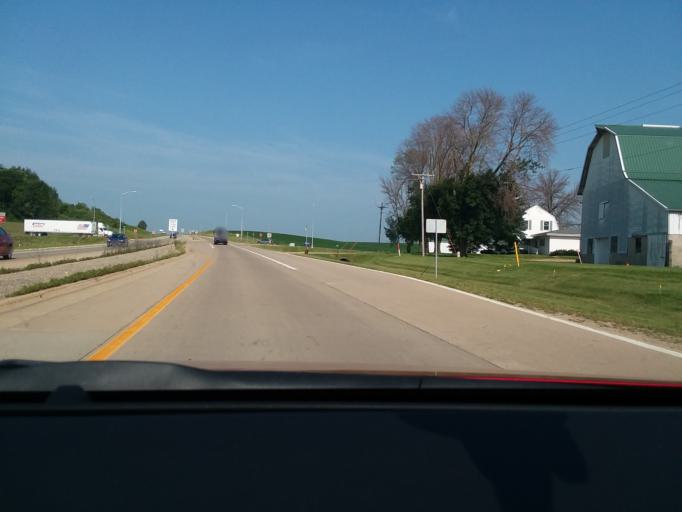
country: US
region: Wisconsin
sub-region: Dane County
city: Windsor
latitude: 43.1949
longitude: -89.3637
